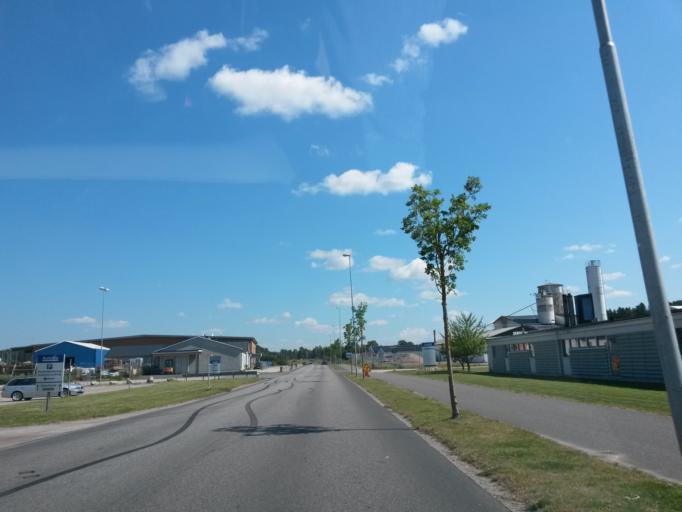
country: SE
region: Vaestra Goetaland
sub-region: Vargarda Kommun
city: Vargarda
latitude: 58.0386
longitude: 12.8001
